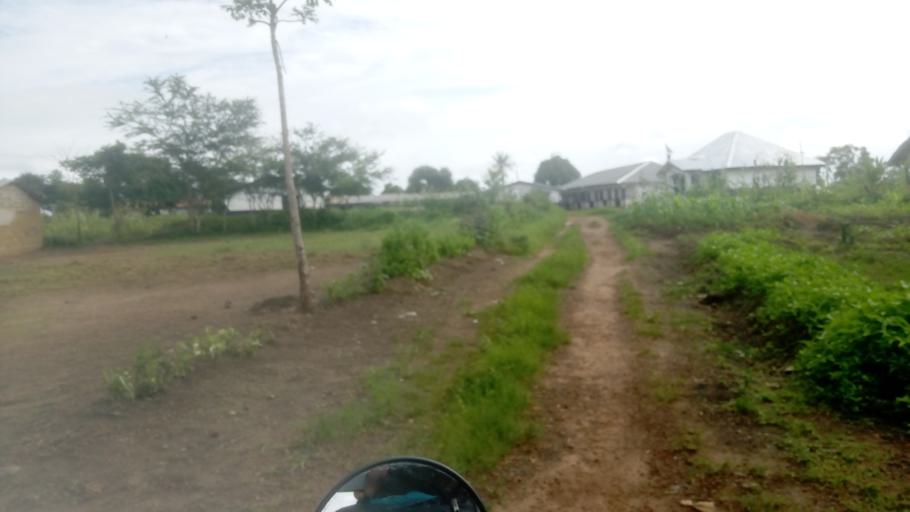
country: SL
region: Northern Province
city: Port Loko
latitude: 8.7076
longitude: -12.6844
